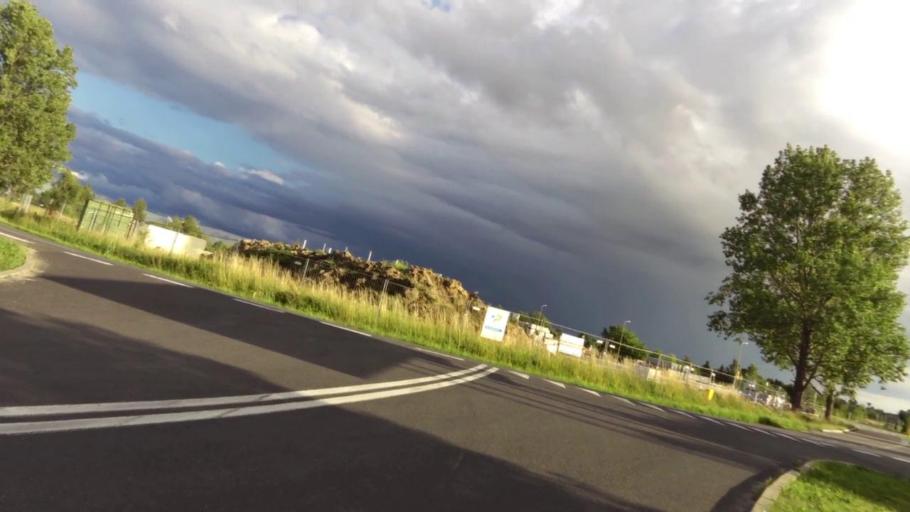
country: PL
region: West Pomeranian Voivodeship
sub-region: Powiat slawienski
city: Darlowo
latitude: 54.4149
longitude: 16.4019
